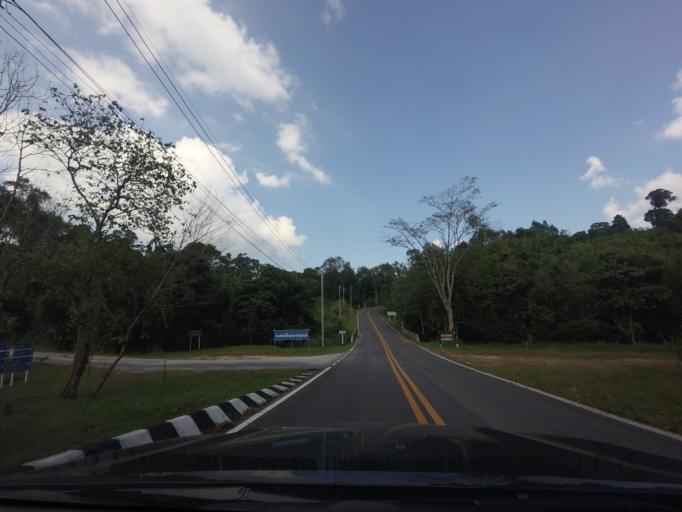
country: TH
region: Phitsanulok
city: Nakhon Thai
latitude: 16.9975
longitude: 101.0089
